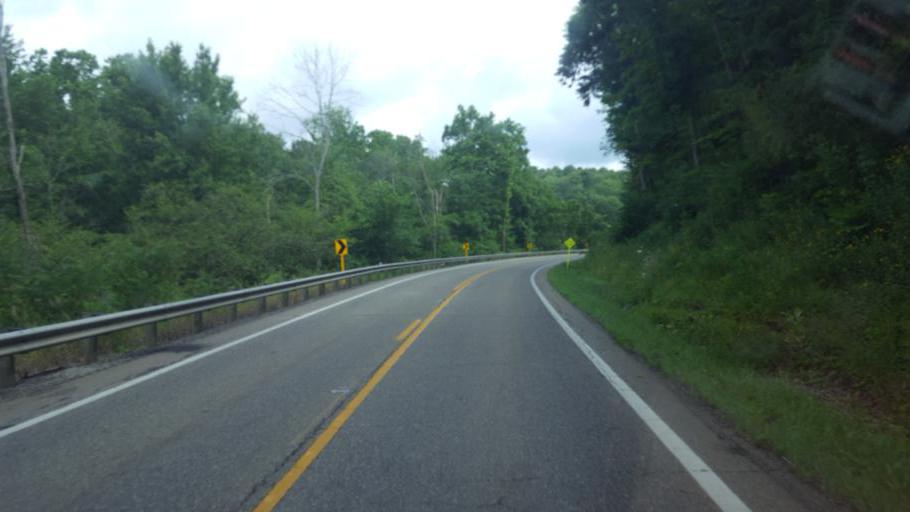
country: US
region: Ohio
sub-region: Columbiana County
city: Salineville
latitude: 40.6367
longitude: -80.8120
